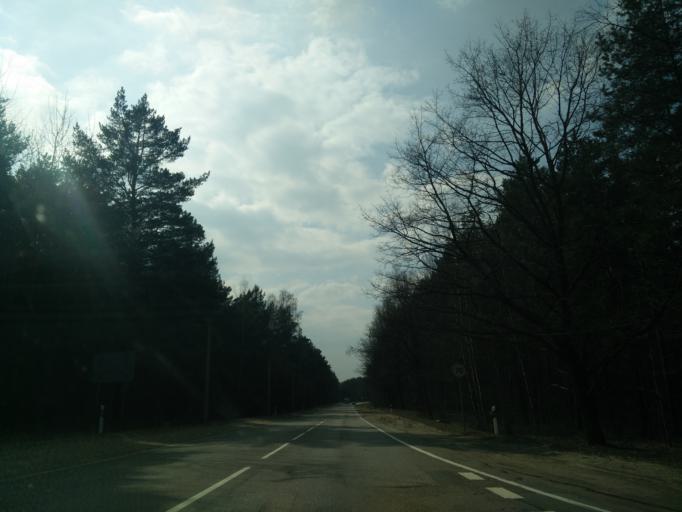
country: LT
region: Vilnius County
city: Lazdynai
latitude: 54.6382
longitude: 25.1770
